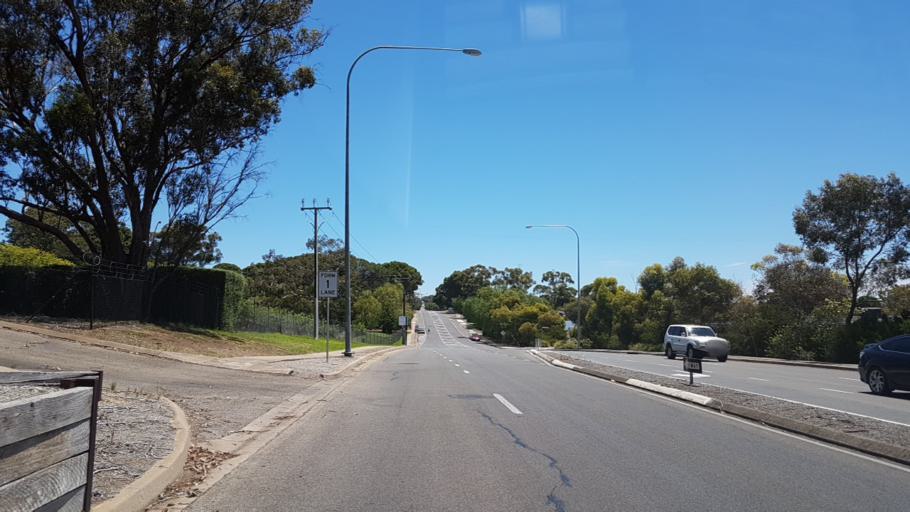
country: AU
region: South Australia
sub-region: Onkaparinga
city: Reynella
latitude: -35.0937
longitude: 138.5461
